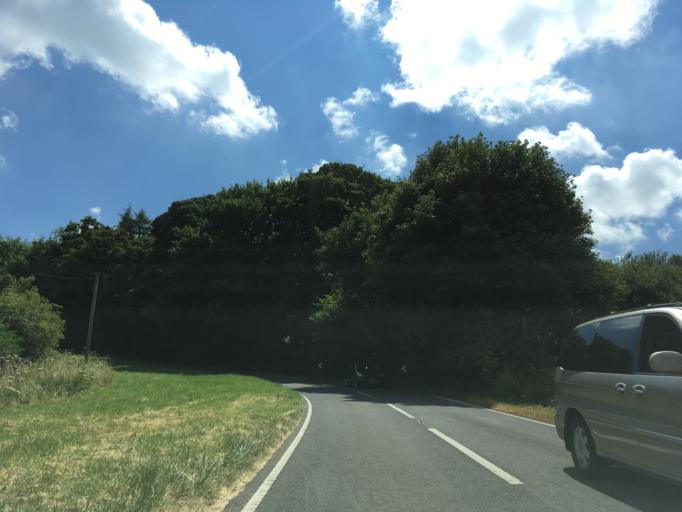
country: GB
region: England
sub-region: Gloucestershire
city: Painswick
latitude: 51.8131
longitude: -2.2042
